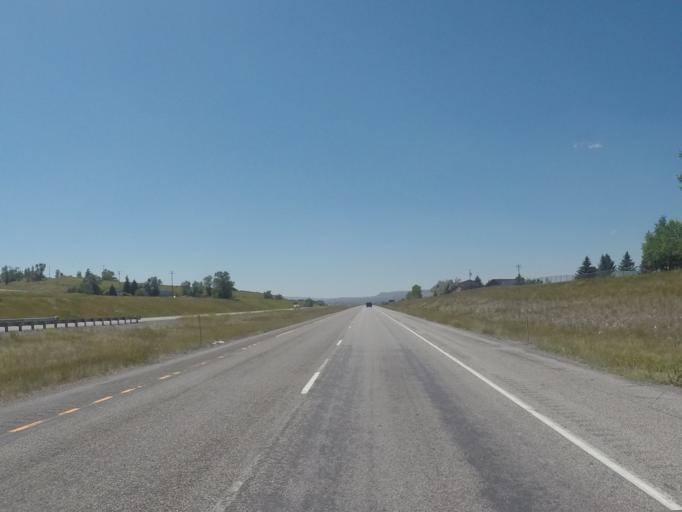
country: US
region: Montana
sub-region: Sweet Grass County
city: Big Timber
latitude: 45.8265
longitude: -109.9487
